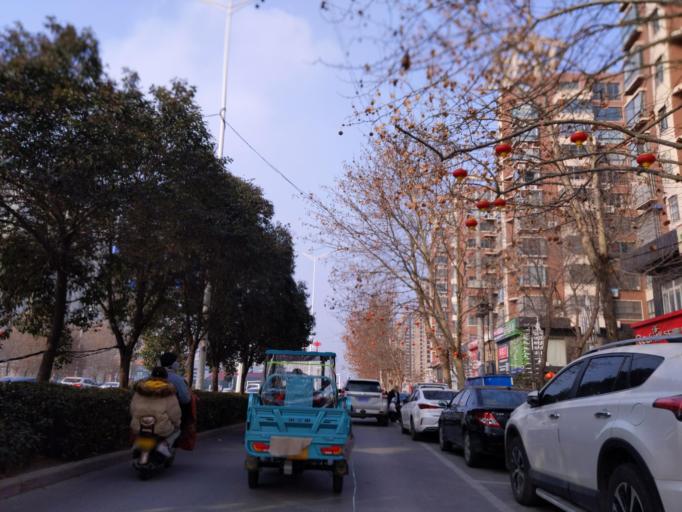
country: CN
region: Henan Sheng
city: Puyang
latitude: 35.7852
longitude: 115.0210
